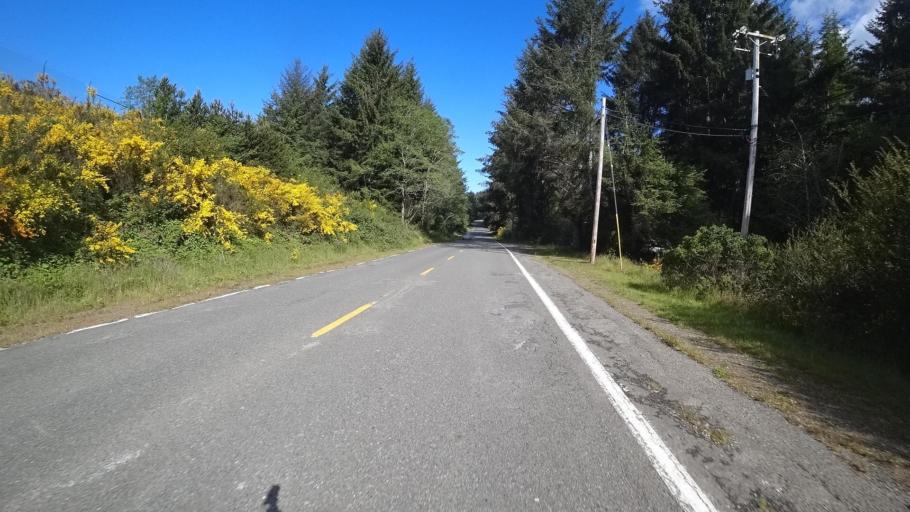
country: US
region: California
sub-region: Humboldt County
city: McKinleyville
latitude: 40.9840
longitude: -124.1040
